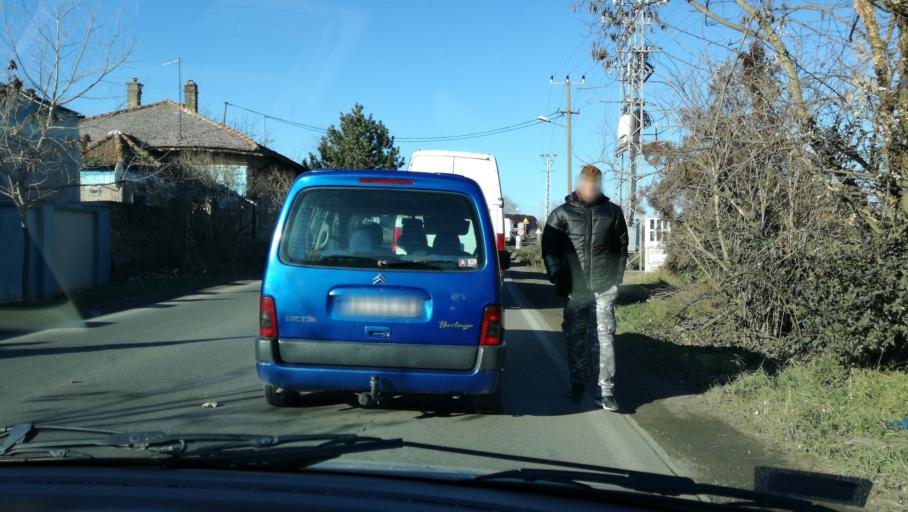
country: RS
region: Autonomna Pokrajina Vojvodina
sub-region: Severnobacki Okrug
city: Subotica
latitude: 46.0843
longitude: 19.6907
